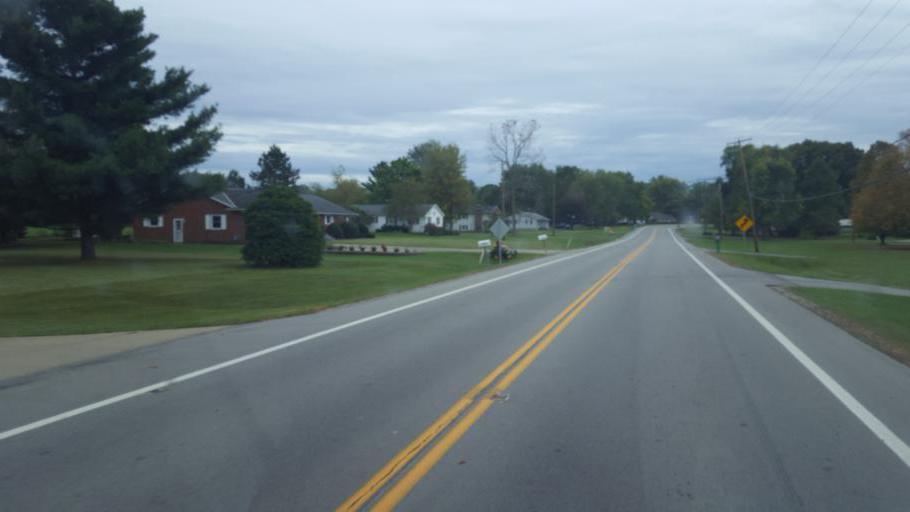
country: US
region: Ohio
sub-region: Huron County
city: Wakeman
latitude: 41.3283
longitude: -82.3609
